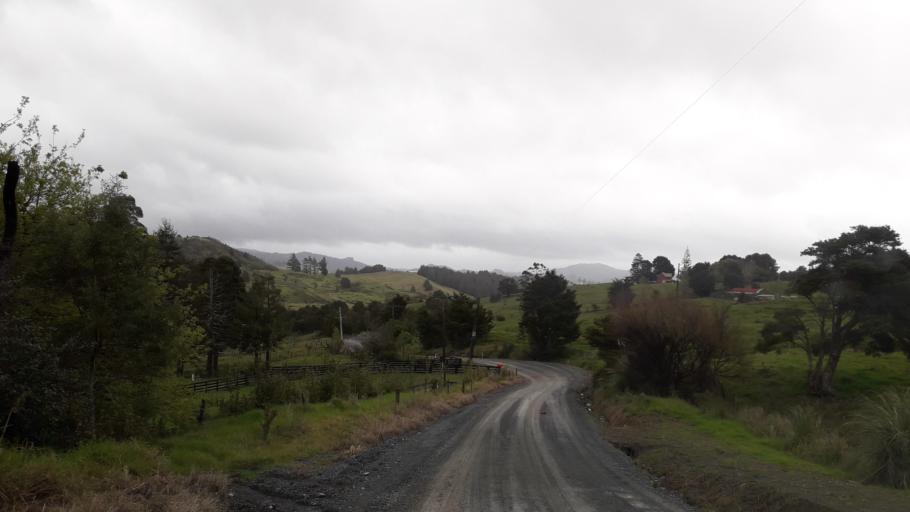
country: NZ
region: Northland
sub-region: Far North District
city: Kerikeri
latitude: -35.1286
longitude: 173.7431
